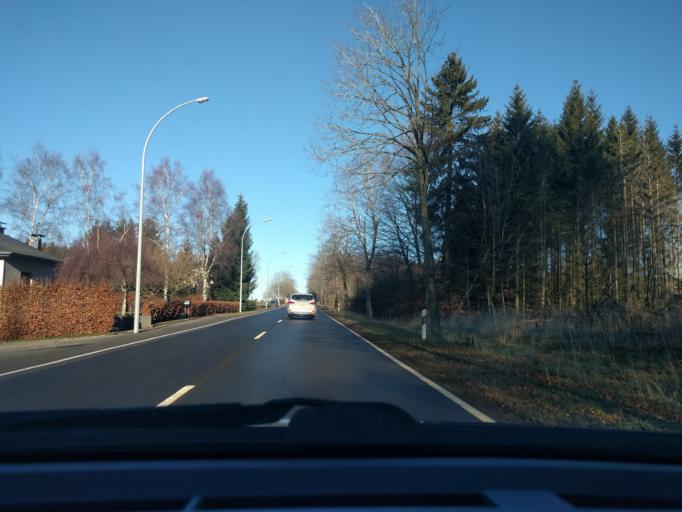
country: LU
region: Diekirch
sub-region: Canton de Clervaux
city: Troisvierges
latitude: 50.1725
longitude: 6.0254
